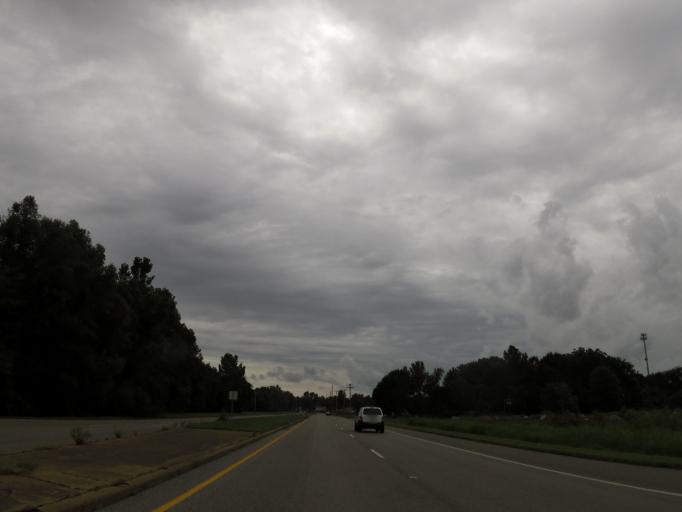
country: US
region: Illinois
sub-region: Alexander County
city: Cairo
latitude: 37.0303
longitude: -89.1865
